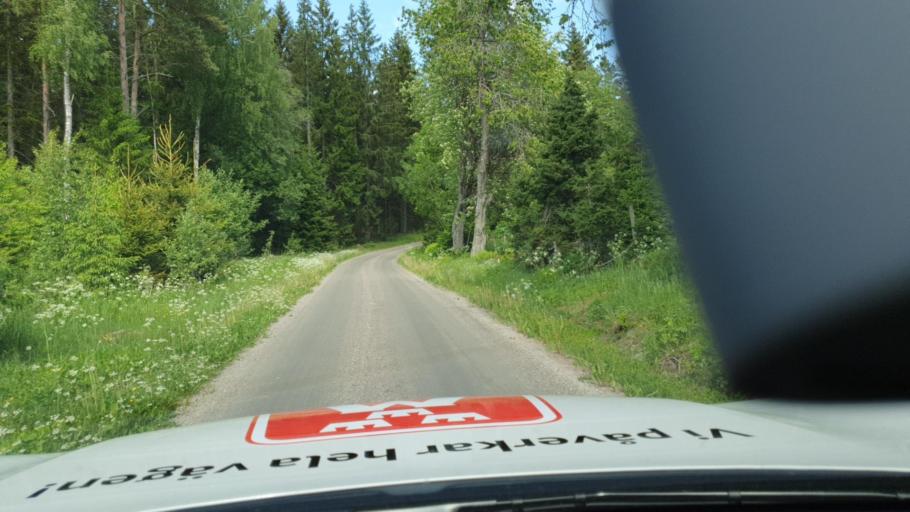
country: SE
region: Vaestra Goetaland
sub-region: Falkopings Kommun
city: Falkoeping
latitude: 58.0459
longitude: 13.6588
